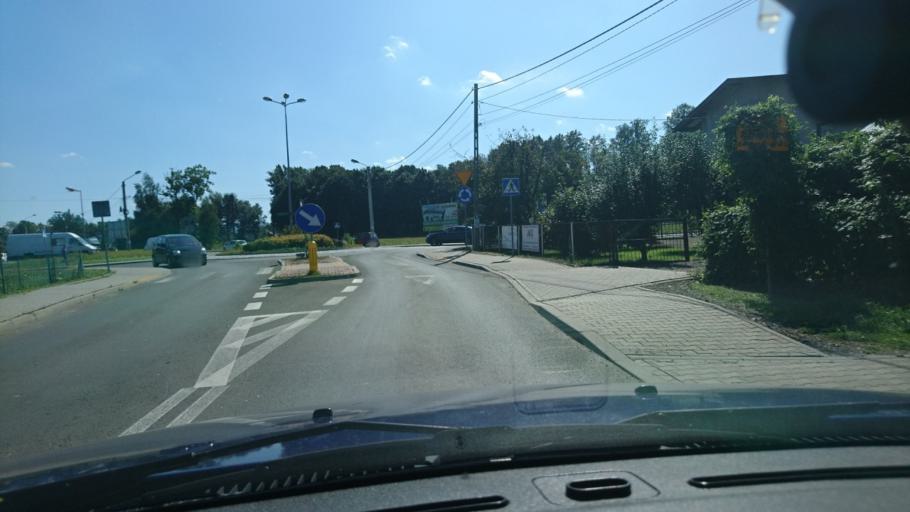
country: PL
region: Silesian Voivodeship
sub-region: Powiat bielski
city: Mazancowice
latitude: 49.8582
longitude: 18.9768
